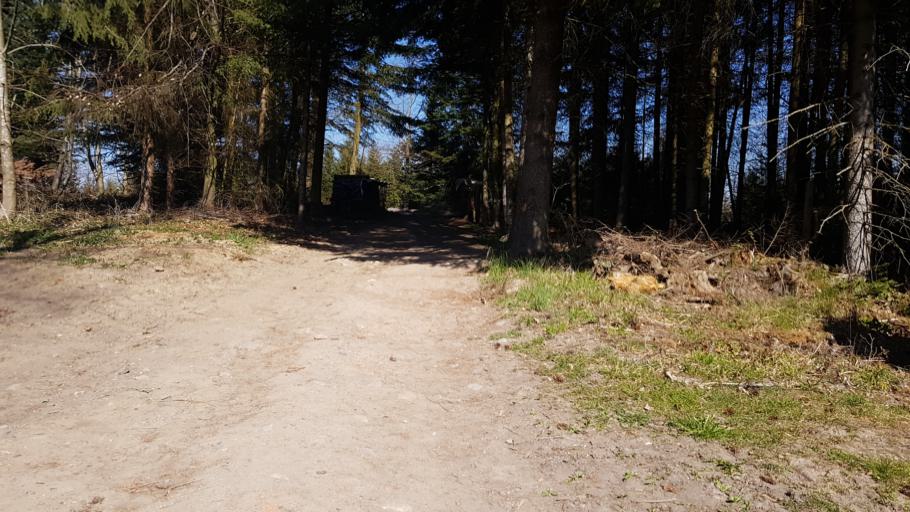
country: CH
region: Aargau
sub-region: Bezirk Kulm
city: Reinach
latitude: 47.2802
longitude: 8.1827
